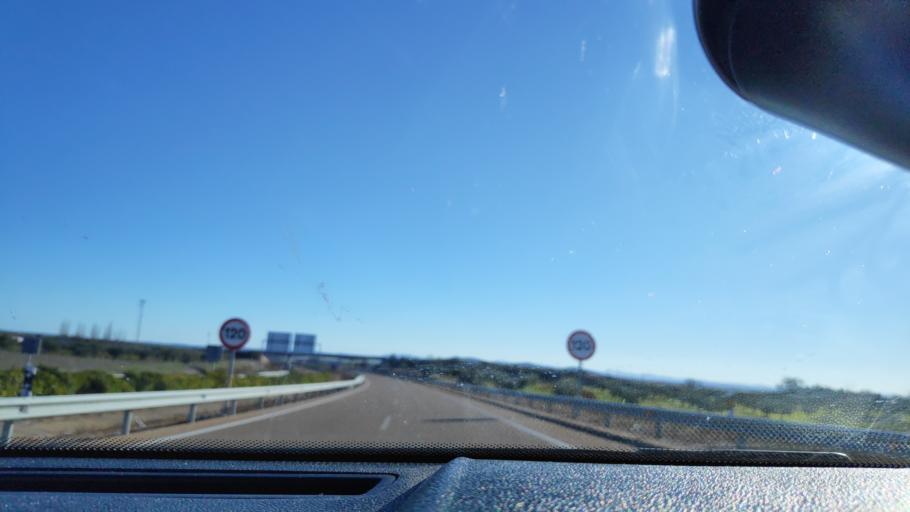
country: ES
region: Extremadura
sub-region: Provincia de Badajoz
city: Puebla de Sancho Perez
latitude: 38.3878
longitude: -6.3404
